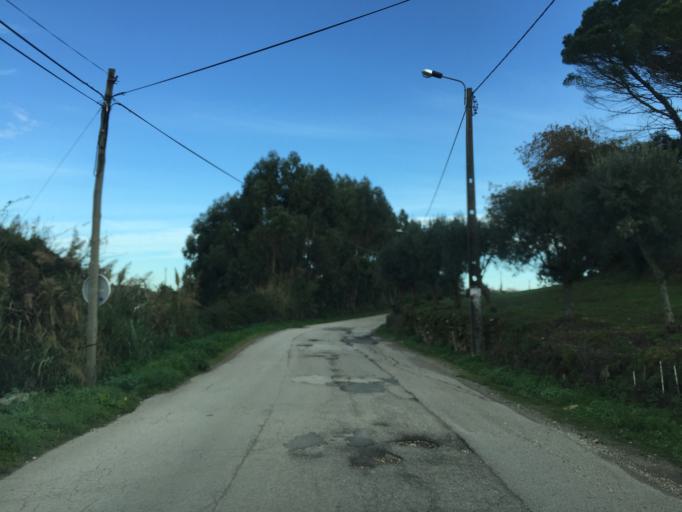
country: PT
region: Lisbon
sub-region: Odivelas
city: Canecas
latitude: 38.8221
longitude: -9.2468
